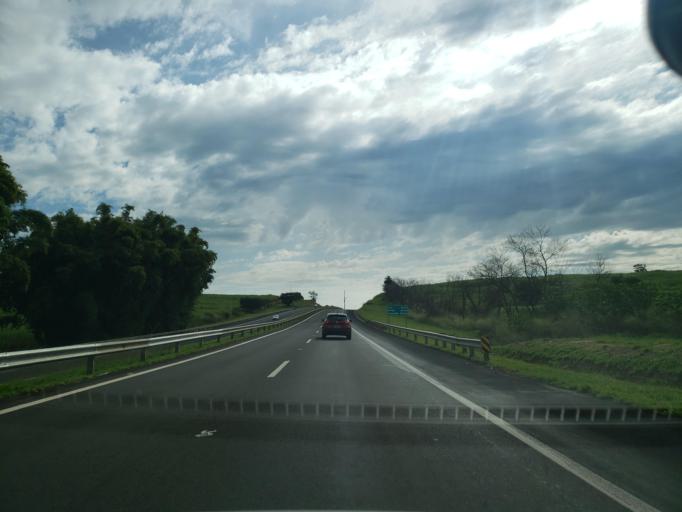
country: BR
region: Sao Paulo
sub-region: Cafelandia
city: Cafelandia
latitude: -21.7997
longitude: -49.6418
